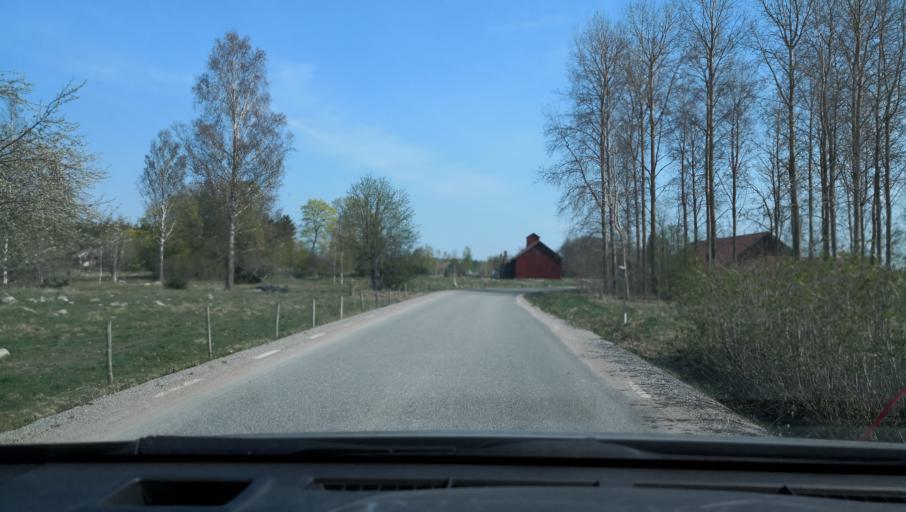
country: SE
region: Vaestmanland
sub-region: Sala Kommun
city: Sala
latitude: 60.0080
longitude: 16.6908
